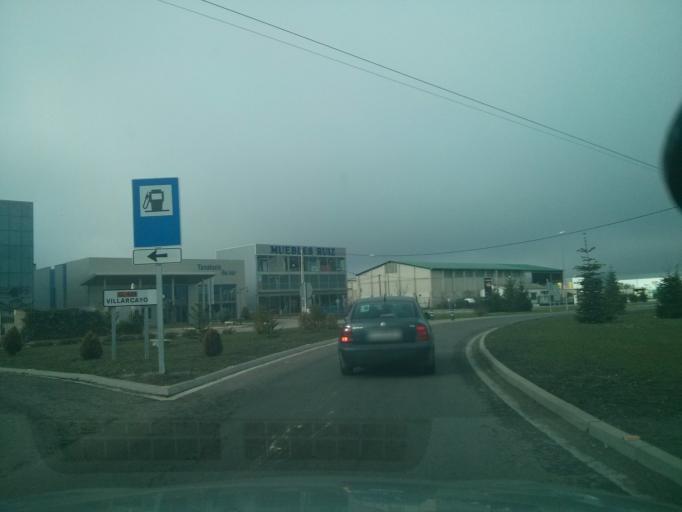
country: ES
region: Castille and Leon
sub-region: Provincia de Burgos
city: Medina de Pomar
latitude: 42.9226
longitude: -3.5793
